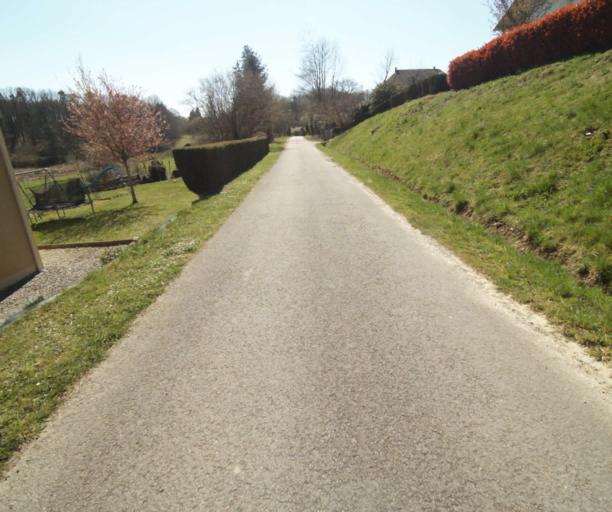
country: FR
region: Limousin
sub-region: Departement de la Correze
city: Saint-Mexant
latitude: 45.2782
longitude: 1.6658
